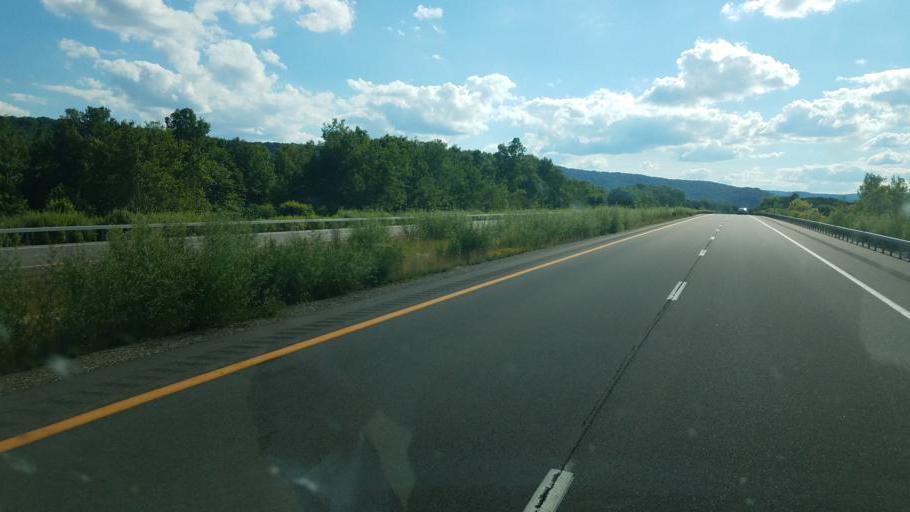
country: US
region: New York
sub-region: Cattaraugus County
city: Allegany
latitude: 42.0884
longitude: -78.5732
